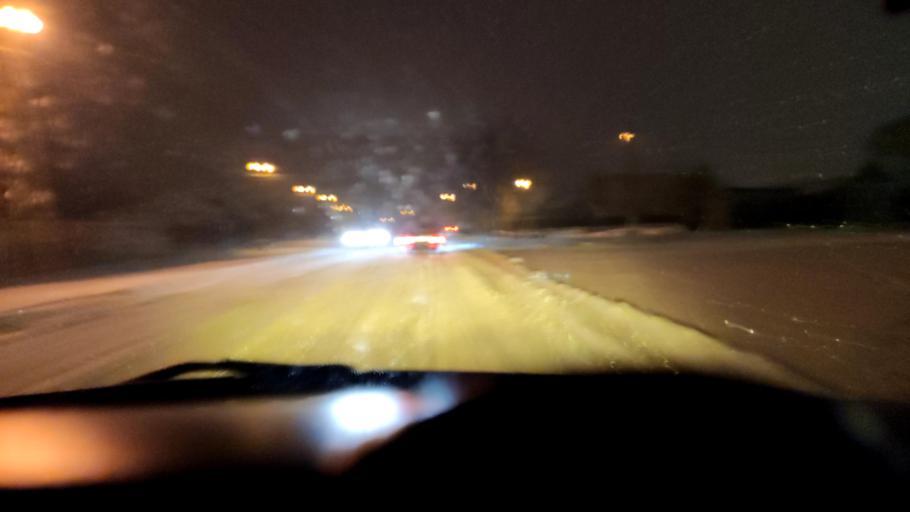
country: RU
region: Voronezj
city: Pridonskoy
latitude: 51.6727
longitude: 39.0775
